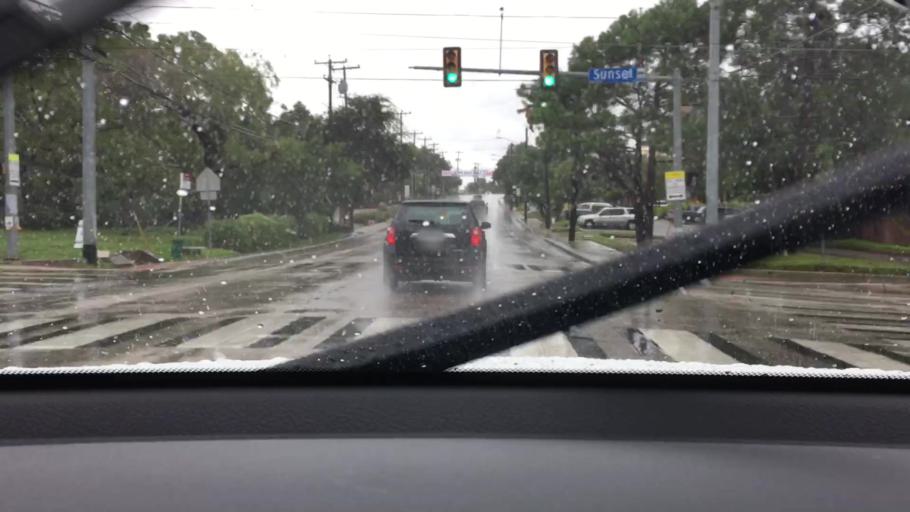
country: US
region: Texas
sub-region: Bexar County
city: Alamo Heights
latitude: 29.5074
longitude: -98.4663
